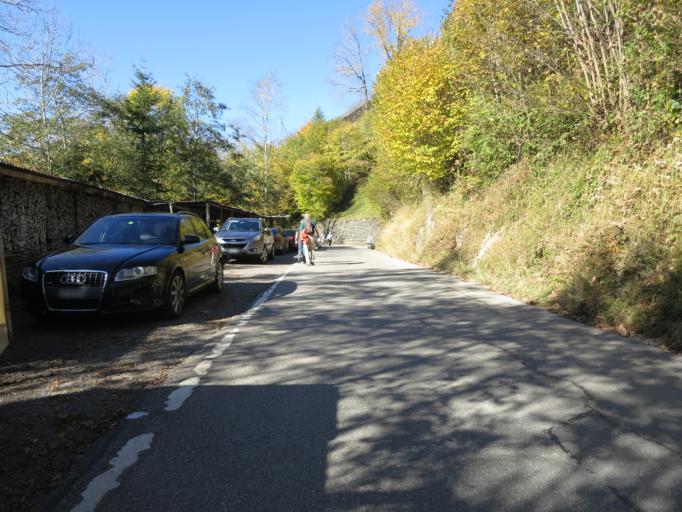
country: CH
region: Schwyz
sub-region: Bezirk March
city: Vorderthal
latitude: 47.0994
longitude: 8.9239
